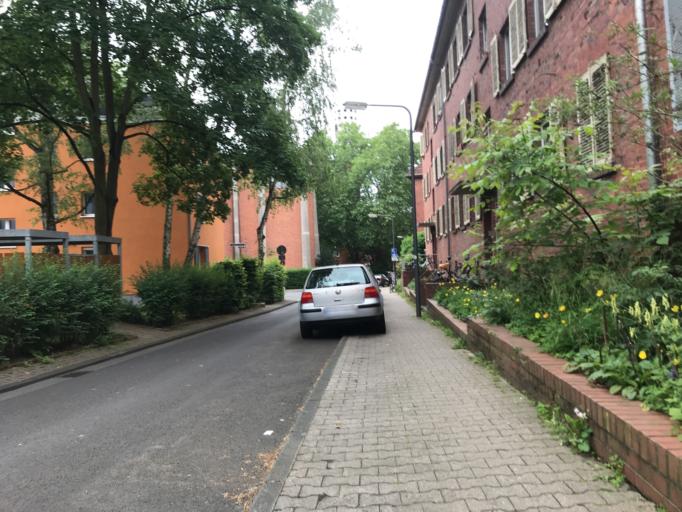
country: DE
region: Hesse
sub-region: Regierungsbezirk Darmstadt
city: Frankfurt am Main
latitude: 50.1319
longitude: 8.6967
